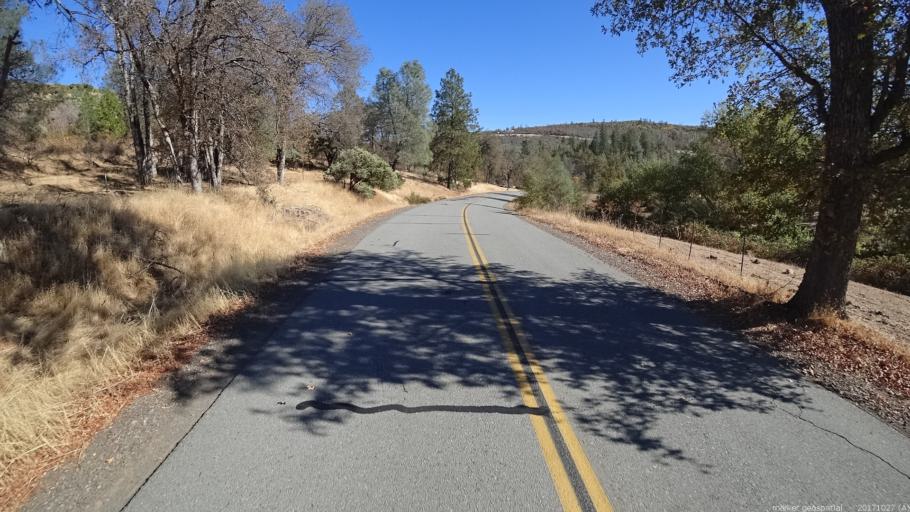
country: US
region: California
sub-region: Shasta County
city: Shingletown
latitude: 40.7725
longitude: -121.9644
